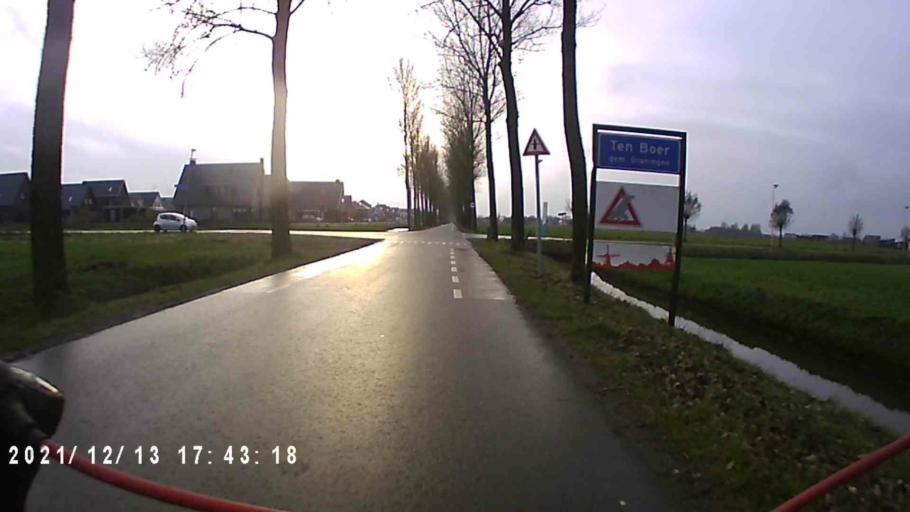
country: NL
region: Groningen
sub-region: Gemeente Bedum
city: Bedum
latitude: 53.2848
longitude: 6.7048
